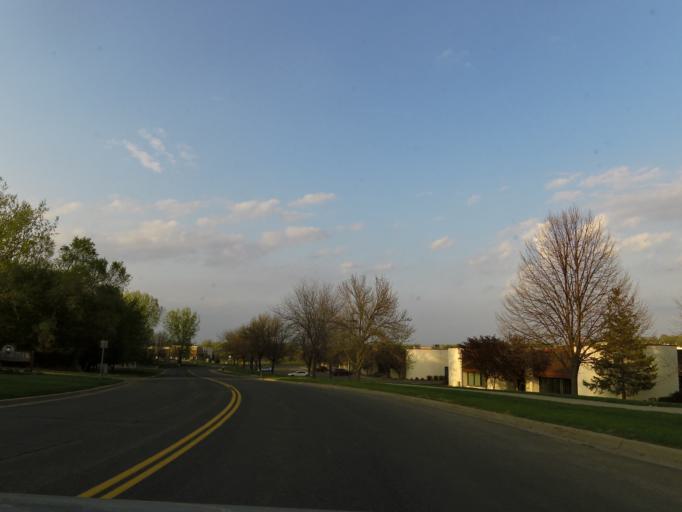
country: US
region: Minnesota
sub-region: Dakota County
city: Eagan
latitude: 44.8193
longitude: -93.2129
